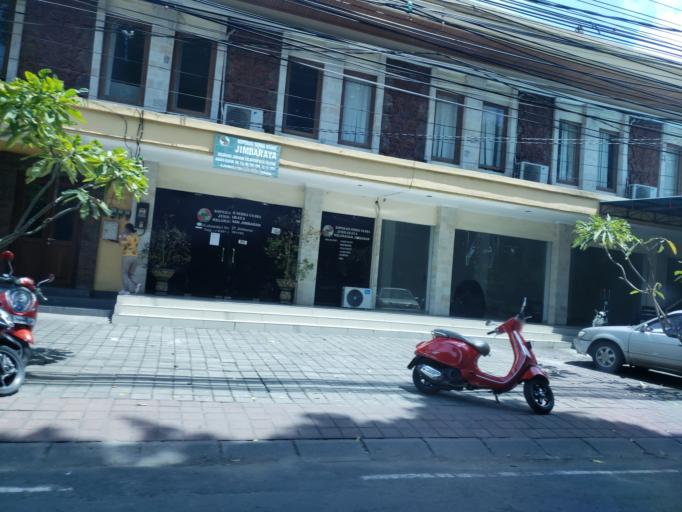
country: ID
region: Bali
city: Kelanabian
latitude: -8.7723
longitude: 115.1727
